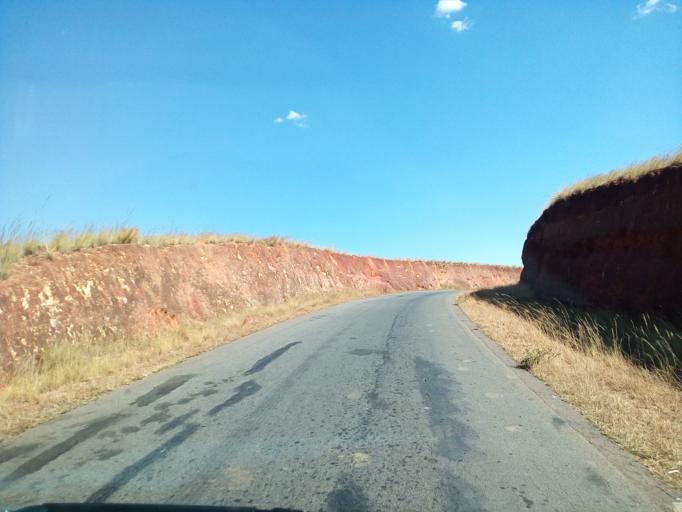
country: MG
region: Betsiboka
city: Maevatanana
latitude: -17.4787
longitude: 46.9964
